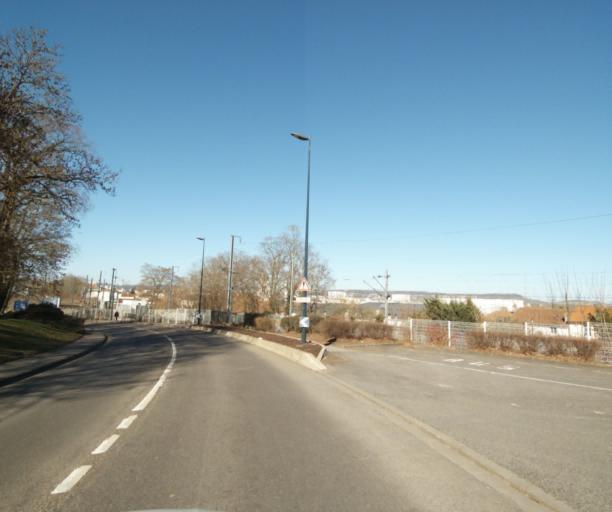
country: FR
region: Lorraine
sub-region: Departement de Meurthe-et-Moselle
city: Jarville-la-Malgrange
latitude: 48.6671
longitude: 6.2083
